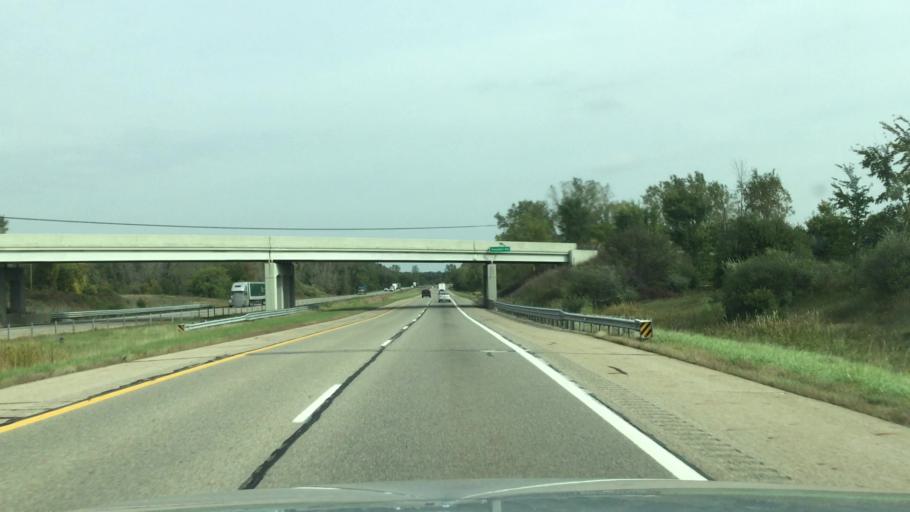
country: US
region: Michigan
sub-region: Shiawassee County
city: Durand
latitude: 42.9502
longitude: -83.9743
